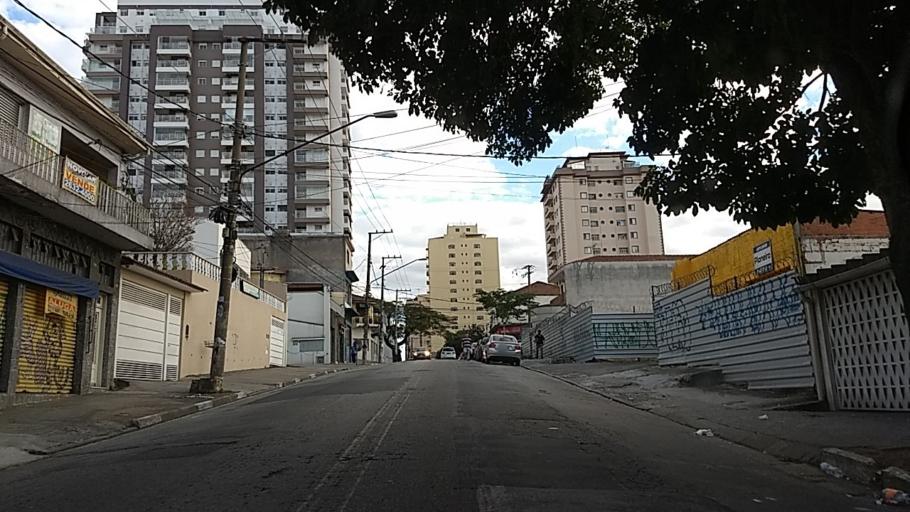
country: BR
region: Sao Paulo
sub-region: Sao Paulo
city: Sao Paulo
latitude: -23.4915
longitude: -46.5966
